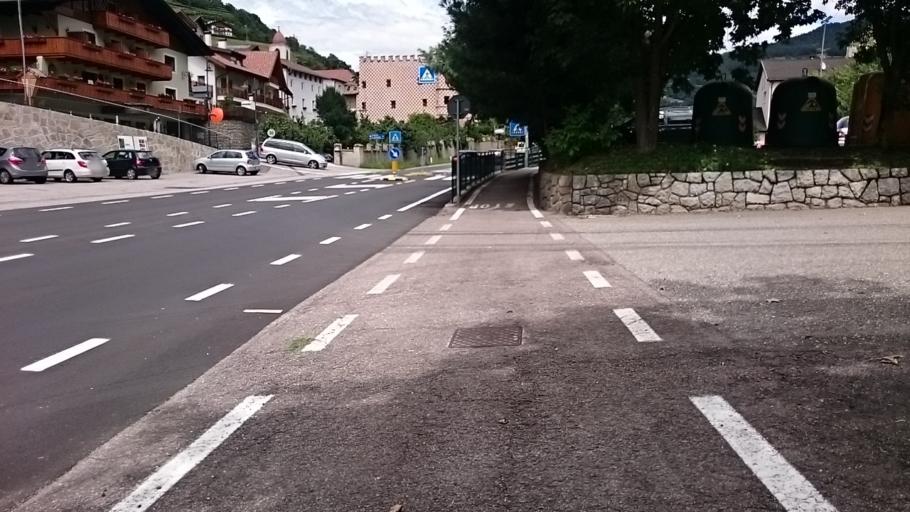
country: IT
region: Trentino-Alto Adige
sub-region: Bolzano
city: Ponte Gardena
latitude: 46.5893
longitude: 11.5245
